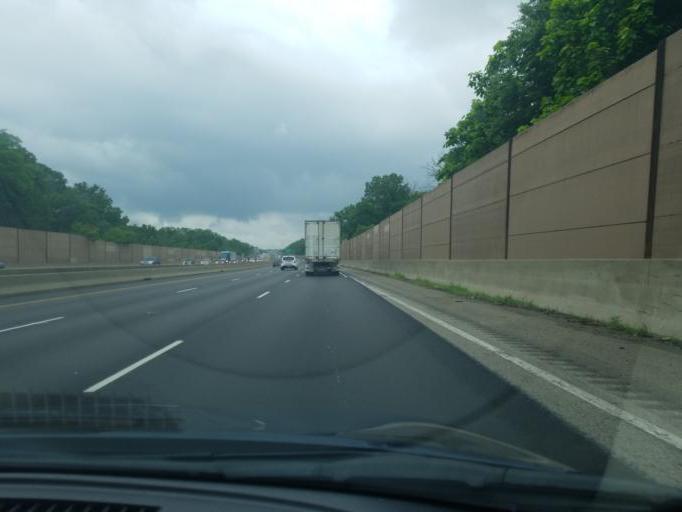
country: US
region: Ohio
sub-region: Hamilton County
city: Kenwood
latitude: 39.2208
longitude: -84.3686
